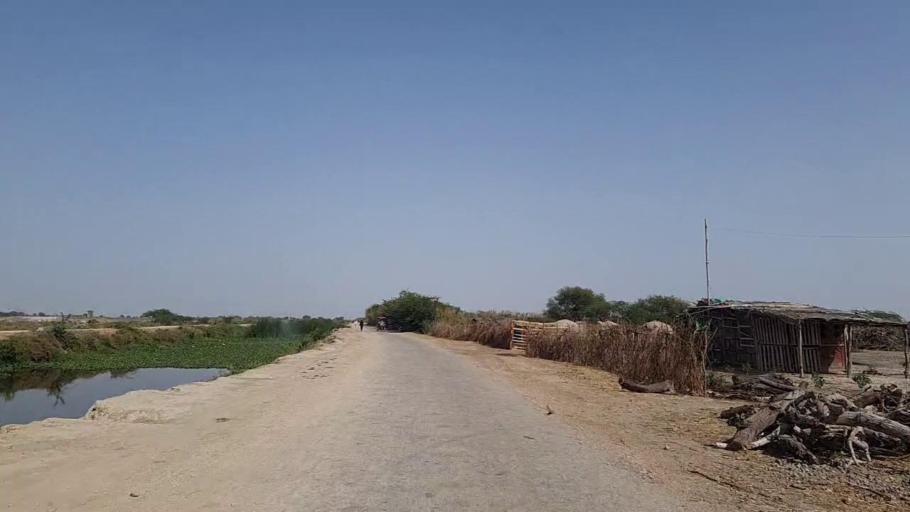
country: PK
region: Sindh
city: Jati
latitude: 24.3606
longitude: 68.2707
